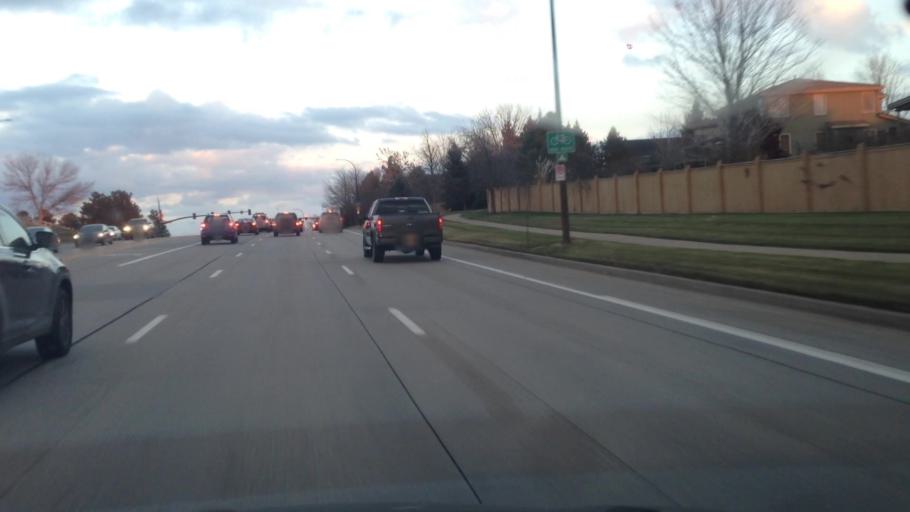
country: US
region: Colorado
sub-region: Douglas County
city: Carriage Club
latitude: 39.5426
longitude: -104.9337
